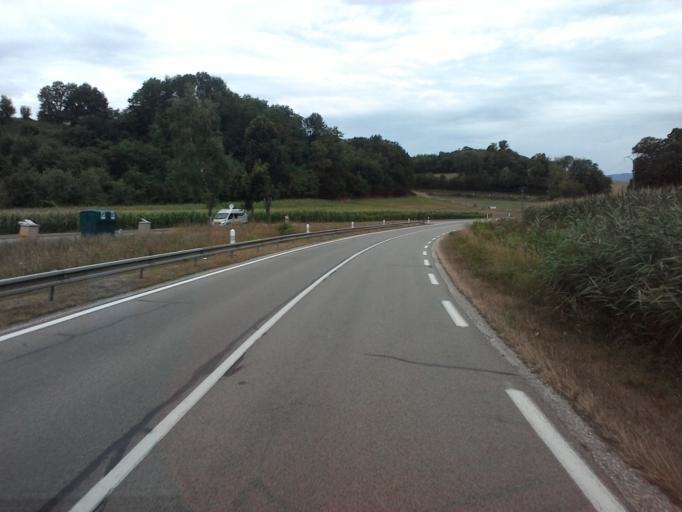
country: FR
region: Rhone-Alpes
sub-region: Departement de l'Isere
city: Faverges-de-la-Tour
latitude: 45.5983
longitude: 5.5341
